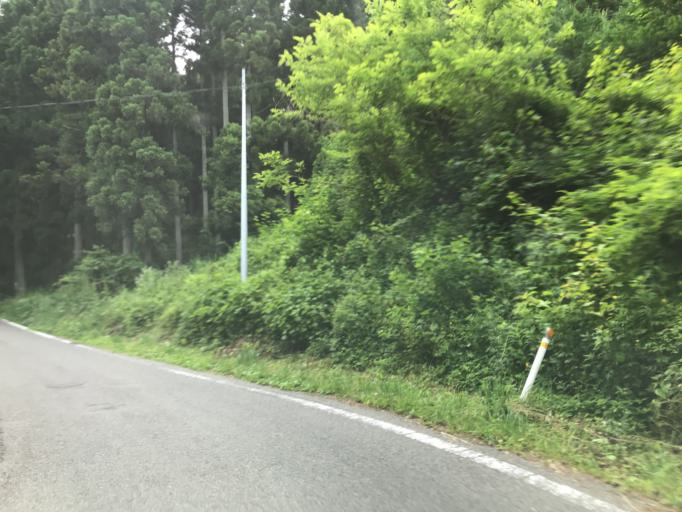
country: JP
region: Fukushima
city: Funehikimachi-funehiki
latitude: 37.4664
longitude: 140.6404
